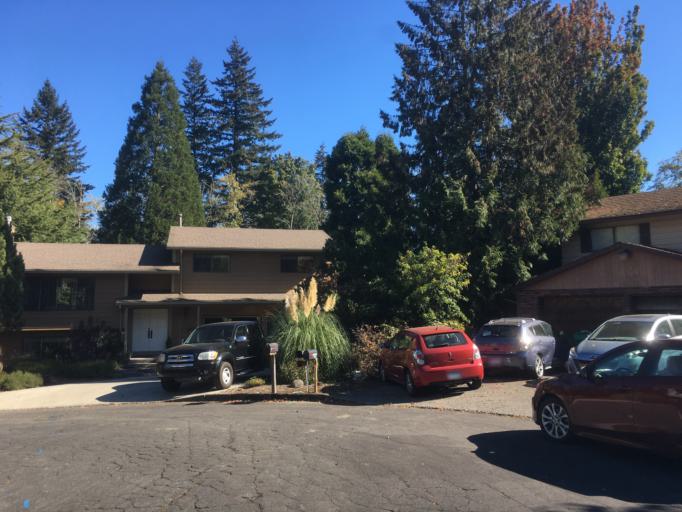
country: US
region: Oregon
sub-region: Multnomah County
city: Gresham
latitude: 45.4826
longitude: -122.4205
